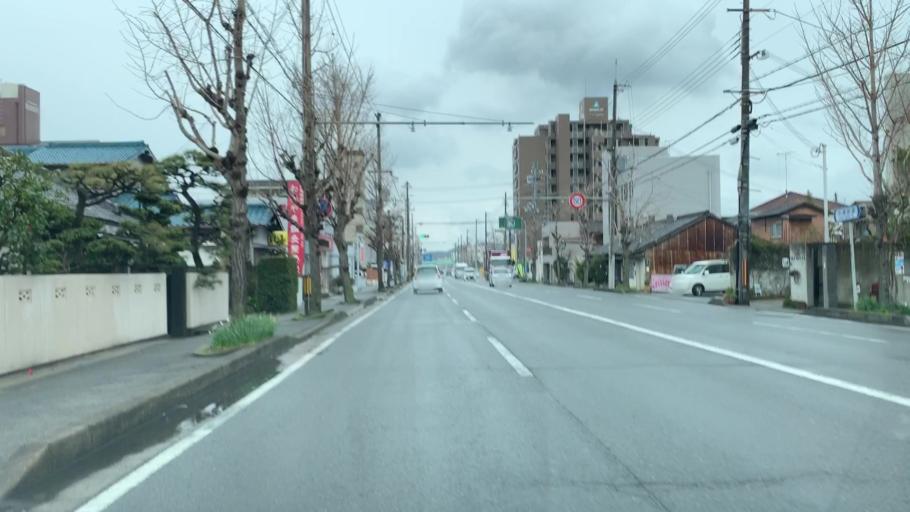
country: JP
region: Wakayama
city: Wakayama-shi
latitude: 34.2223
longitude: 135.1596
